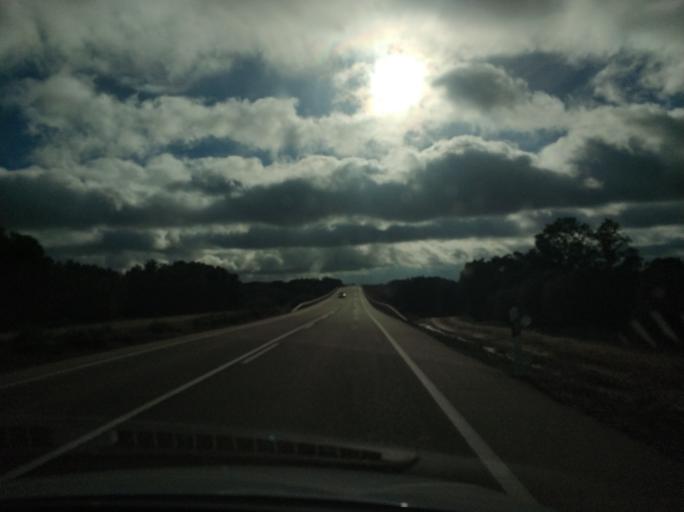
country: ES
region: Castille and Leon
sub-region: Provincia de Soria
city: Fuentecambron
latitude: 41.4935
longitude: -3.3112
